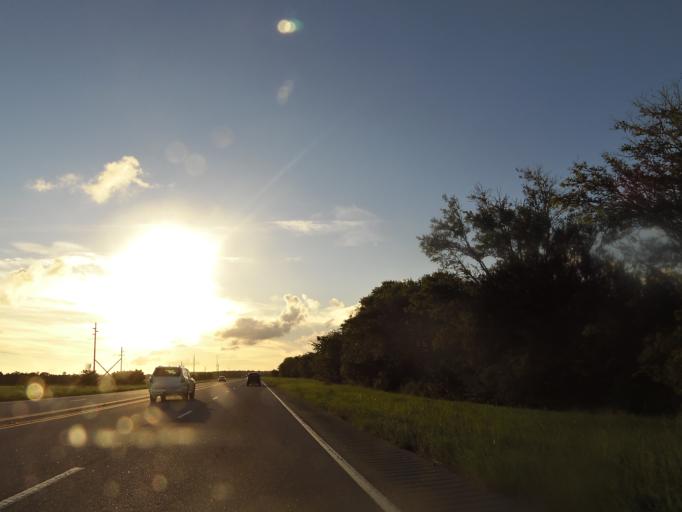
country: US
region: Georgia
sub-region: Glynn County
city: Brunswick
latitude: 31.1095
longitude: -81.5153
